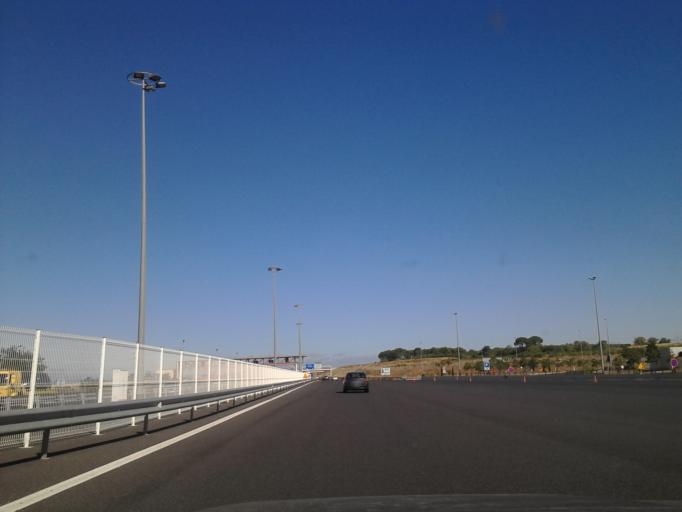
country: FR
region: Languedoc-Roussillon
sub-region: Departement de l'Herault
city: Cers
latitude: 43.3434
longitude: 3.2884
